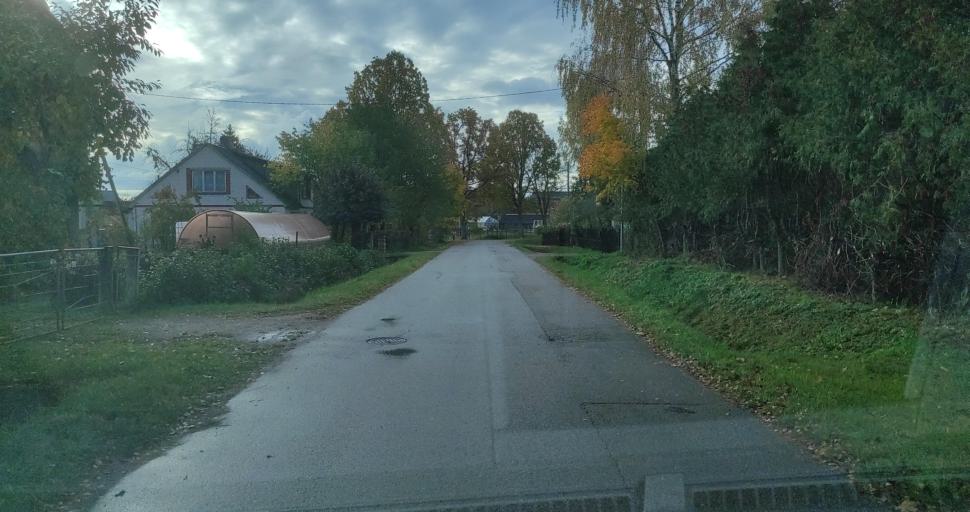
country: LV
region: Skrunda
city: Skrunda
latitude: 56.6721
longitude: 22.0130
